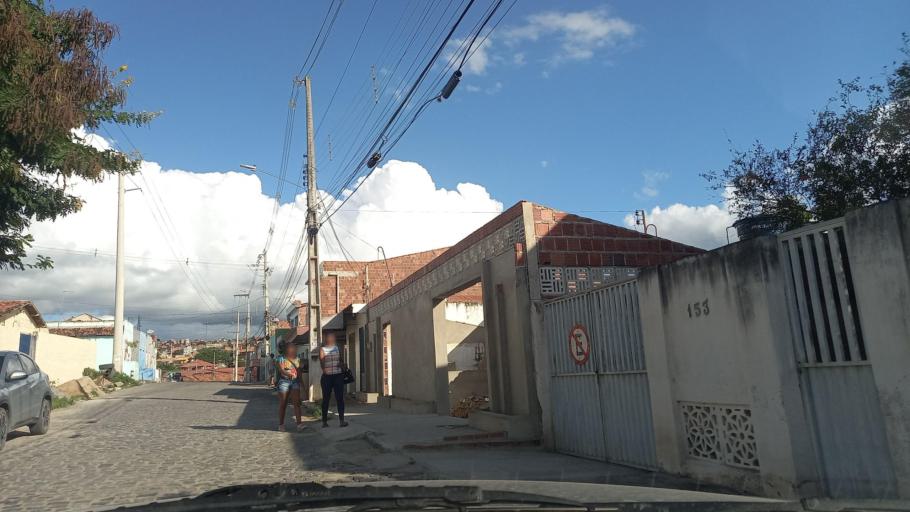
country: BR
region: Pernambuco
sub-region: Gravata
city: Gravata
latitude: -8.2031
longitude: -35.5735
